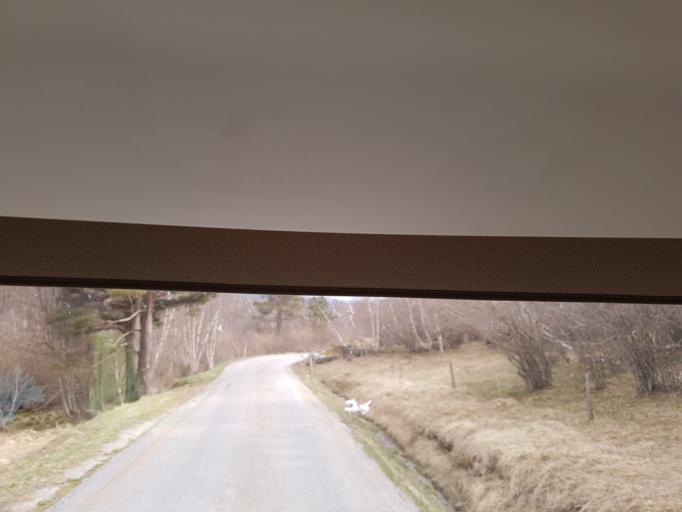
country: FR
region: Languedoc-Roussillon
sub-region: Departement de l'Aude
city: Quillan
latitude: 42.6656
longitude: 2.1293
